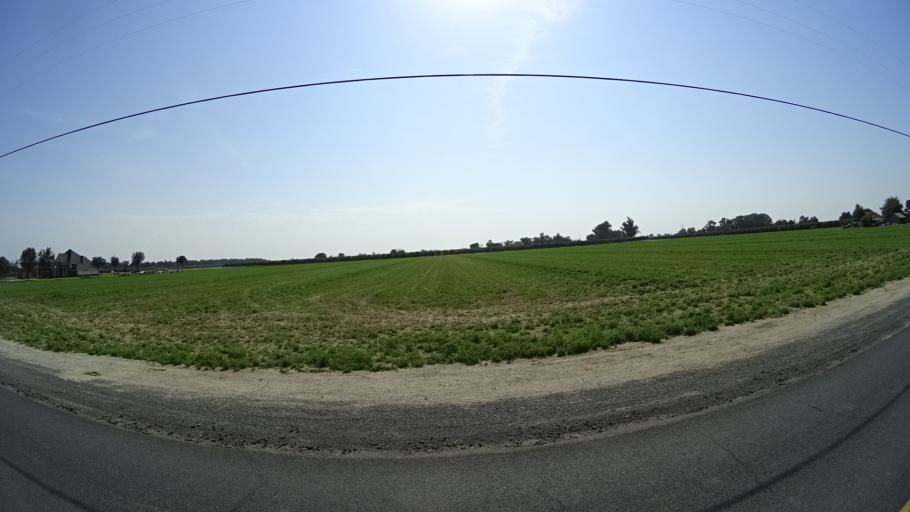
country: US
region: California
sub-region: Kings County
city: Lemoore
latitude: 36.3295
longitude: -119.8514
